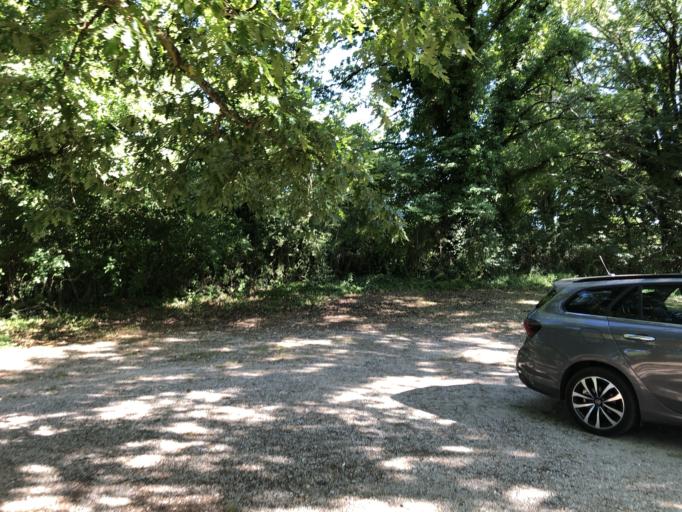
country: IT
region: Tuscany
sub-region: Province of Pisa
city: Castelnuovo di Val di Cecina
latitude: 43.2043
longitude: 10.9253
